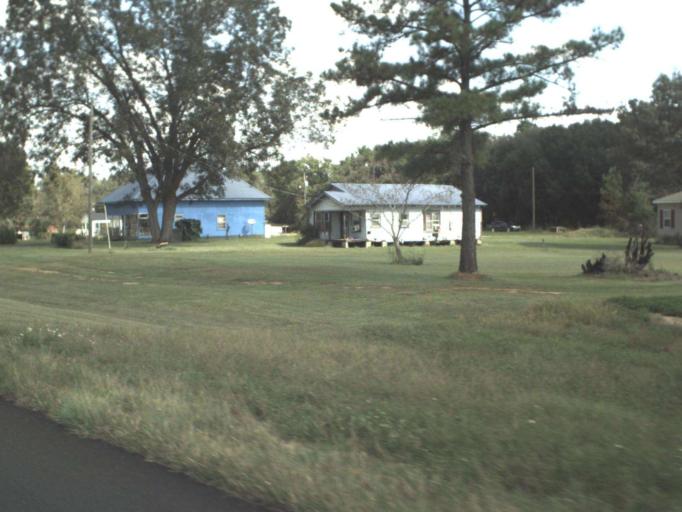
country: US
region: Florida
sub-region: Jackson County
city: Graceville
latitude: 30.9907
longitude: -85.4078
